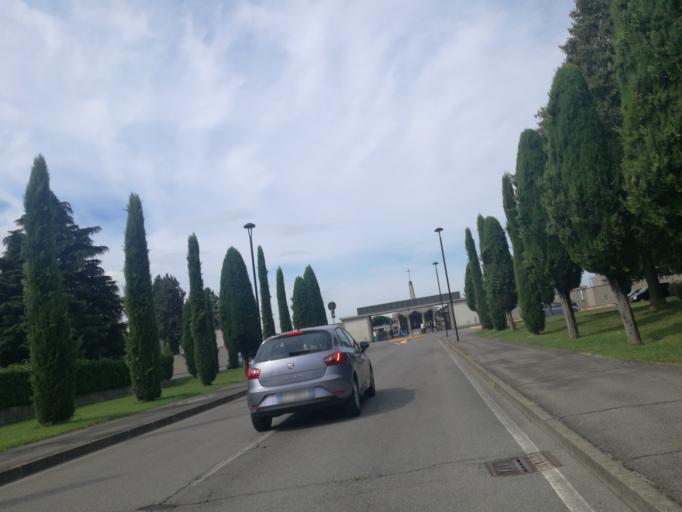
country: IT
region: Lombardy
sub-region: Provincia di Bergamo
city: Calusco d'Adda
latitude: 45.6877
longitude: 9.4632
